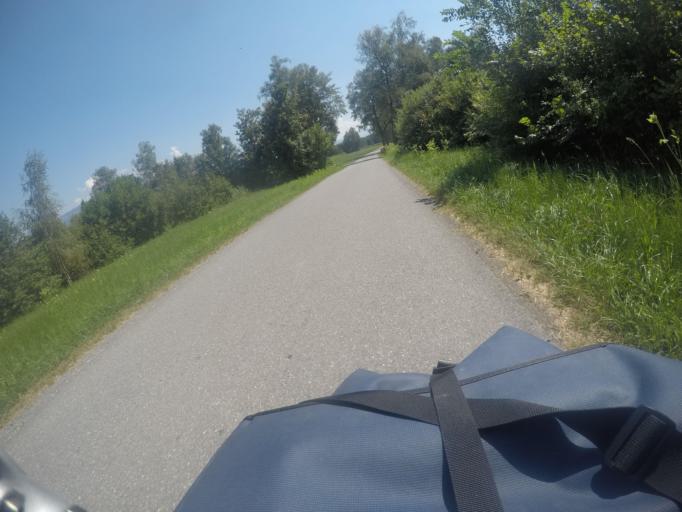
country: AT
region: Vorarlberg
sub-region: Politischer Bezirk Feldkirch
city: Koblach
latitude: 47.3534
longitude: 9.5761
